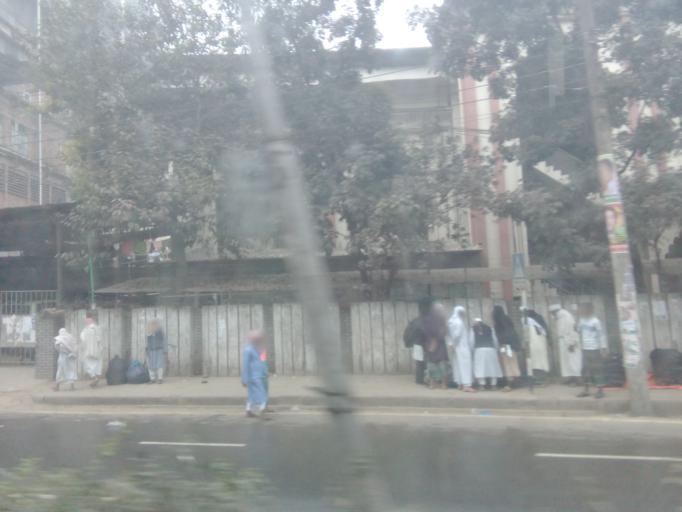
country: BD
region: Dhaka
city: Paltan
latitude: 23.7369
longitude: 90.4039
